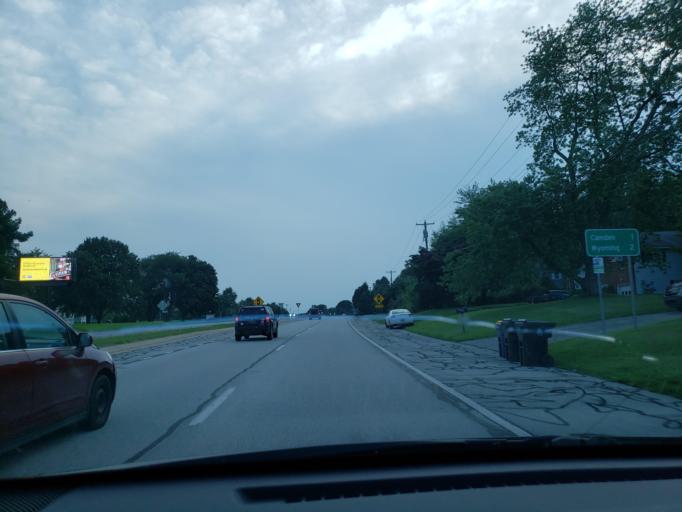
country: US
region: Delaware
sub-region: Kent County
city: Highland Acres
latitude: 39.1178
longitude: -75.5175
